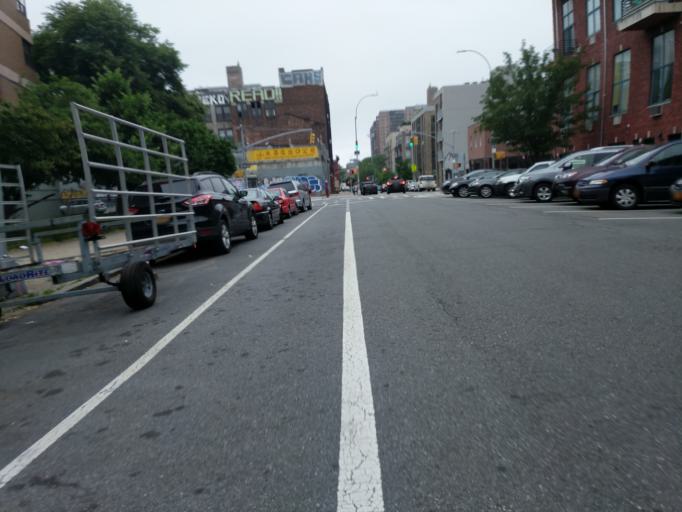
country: US
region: New York
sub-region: Queens County
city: Long Island City
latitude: 40.7089
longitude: -73.9468
